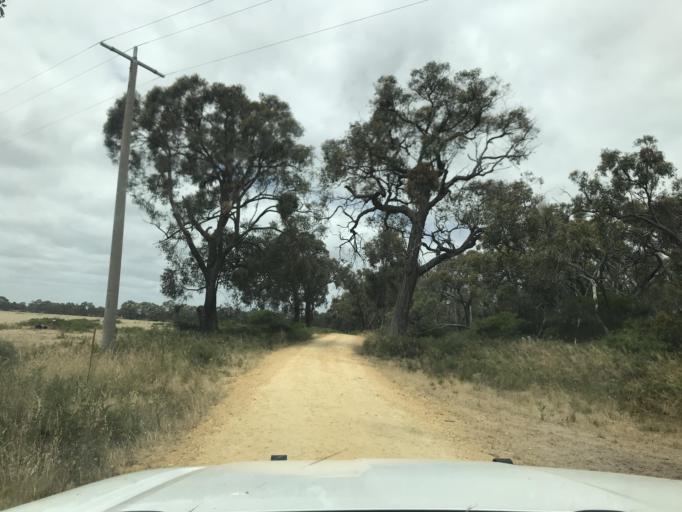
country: AU
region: South Australia
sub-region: Naracoorte and Lucindale
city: Naracoorte
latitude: -37.0051
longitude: 141.3420
